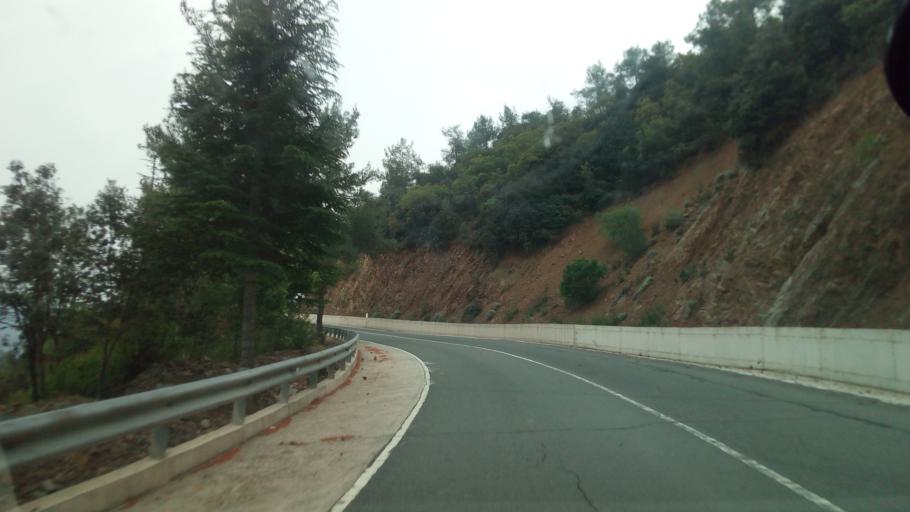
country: CY
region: Lefkosia
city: Lefka
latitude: 34.9975
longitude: 32.7349
